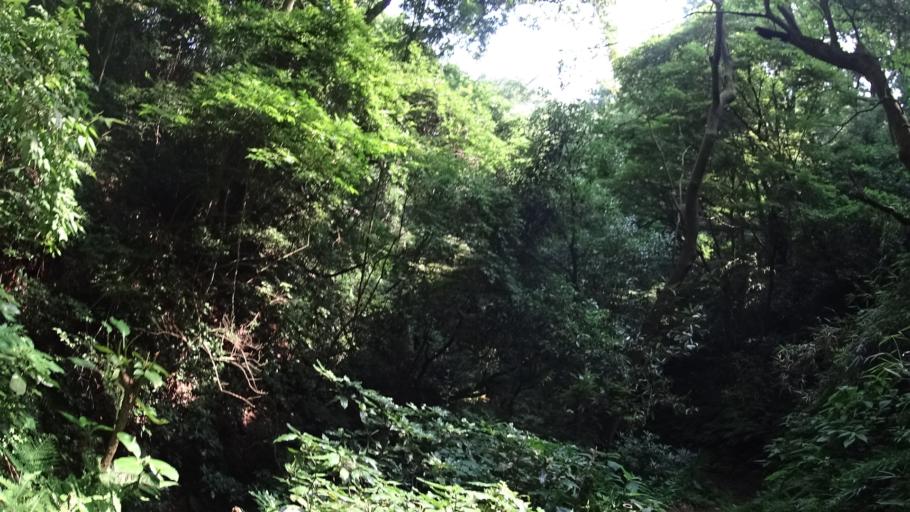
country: JP
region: Kanagawa
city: Zushi
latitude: 35.3040
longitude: 139.6049
